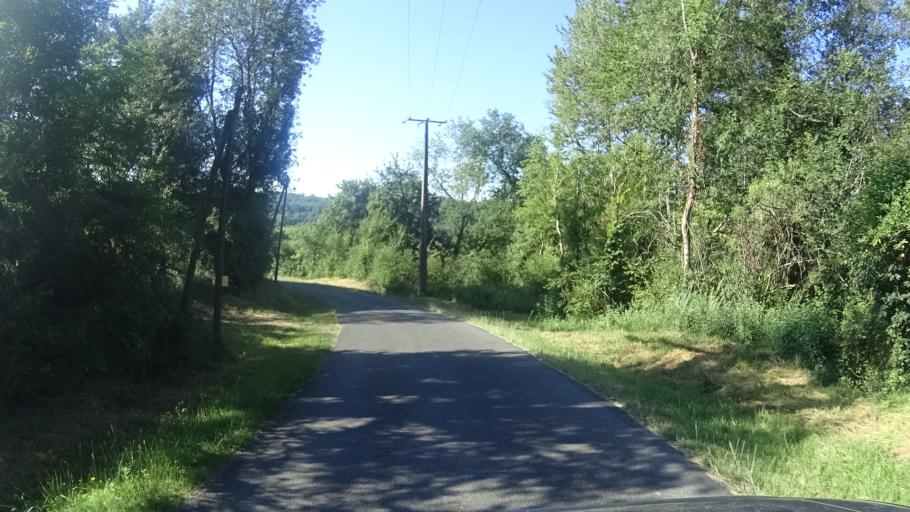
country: FR
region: Aquitaine
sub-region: Departement de la Dordogne
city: Sourzac
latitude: 45.0201
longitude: 0.3992
